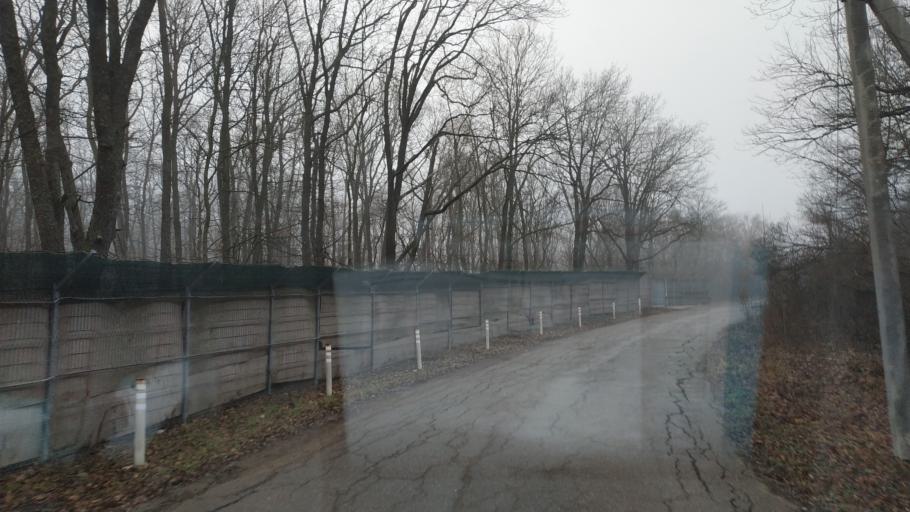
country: MD
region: Laloveni
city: Ialoveni
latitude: 46.9500
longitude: 28.7005
